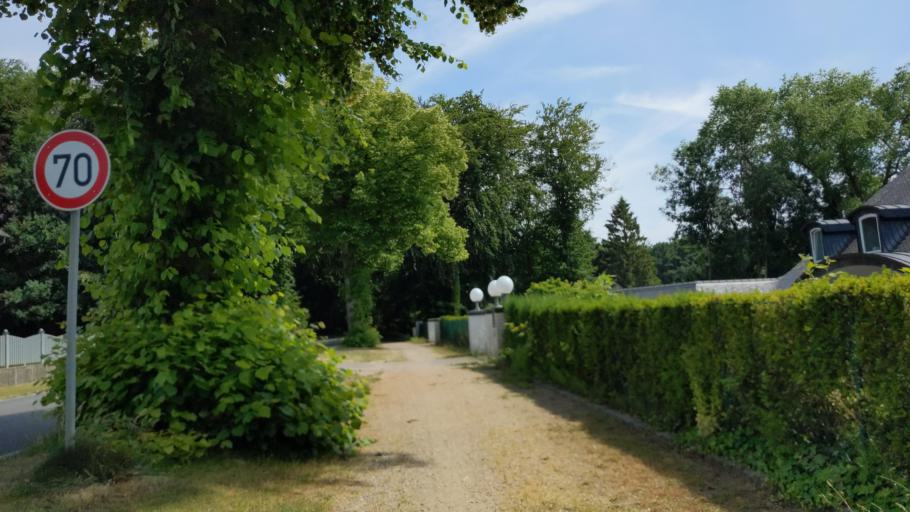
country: DE
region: Schleswig-Holstein
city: Malente
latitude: 54.1837
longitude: 10.6004
